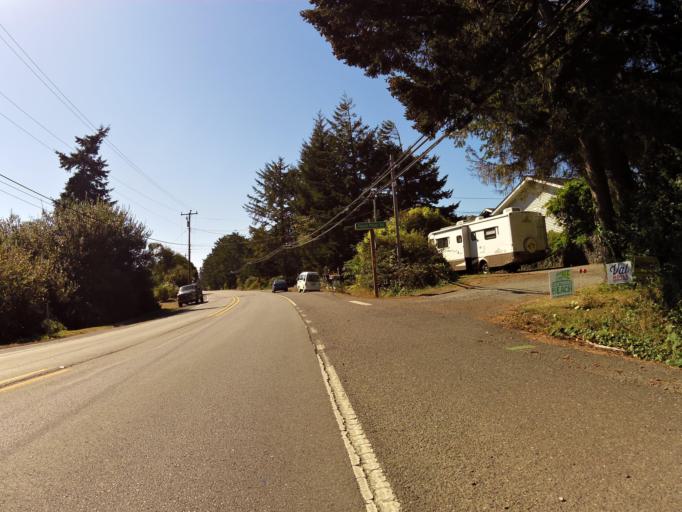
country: US
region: Oregon
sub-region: Coos County
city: Barview
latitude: 43.3556
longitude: -124.3112
